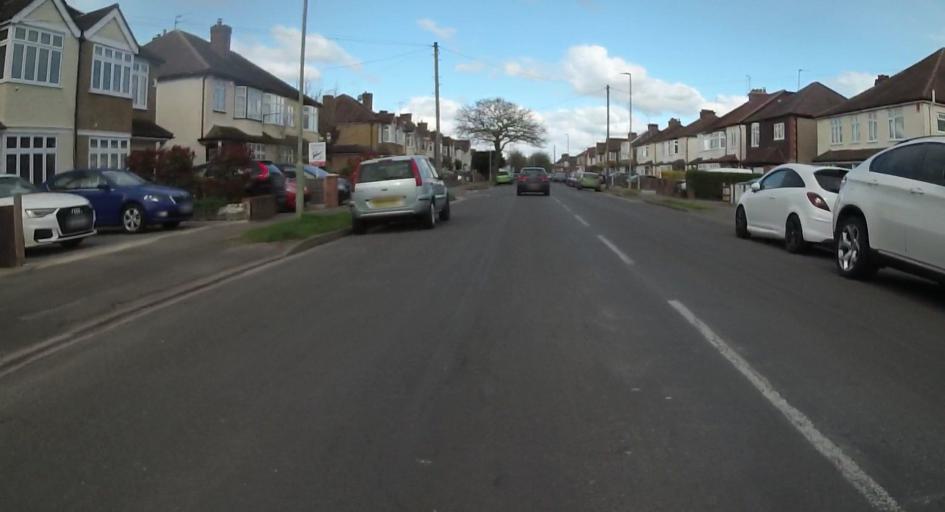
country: GB
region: England
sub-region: Surrey
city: West Byfleet
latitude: 51.3460
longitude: -0.5014
